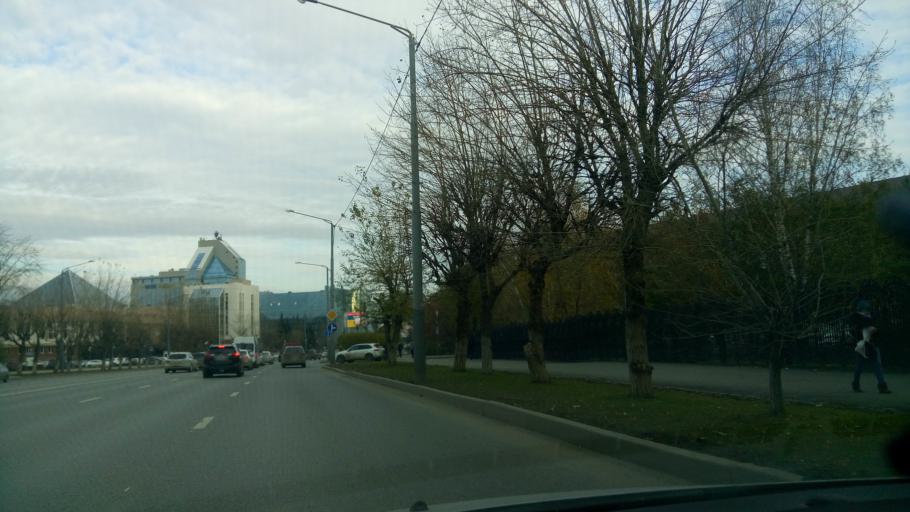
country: RU
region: Tjumen
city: Tyumen
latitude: 57.1355
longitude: 65.5661
